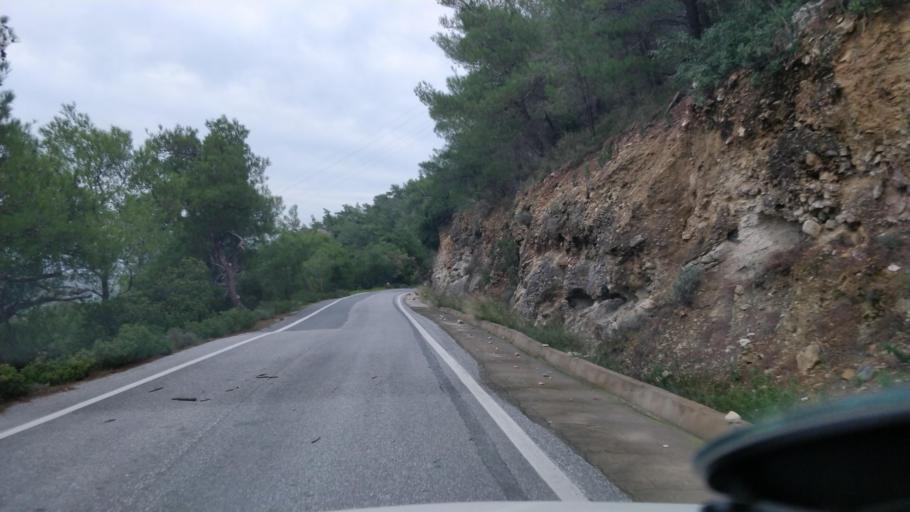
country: GR
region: Crete
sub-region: Nomos Lasithiou
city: Kritsa
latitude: 35.1017
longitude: 25.6998
